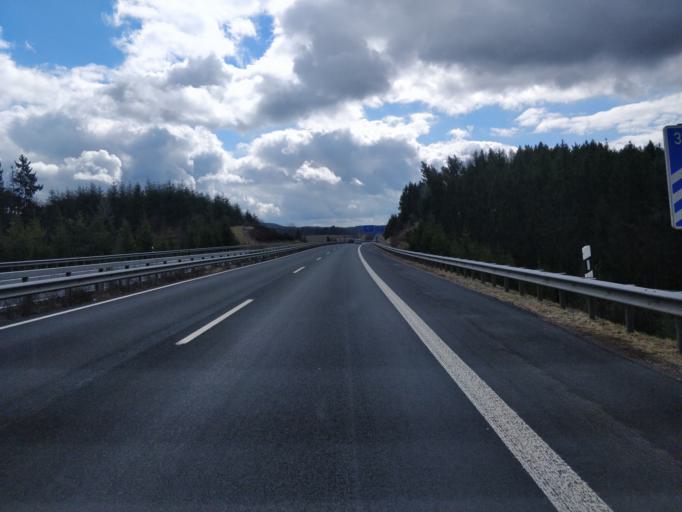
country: DE
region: Rheinland-Pfalz
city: Mehren
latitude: 50.1989
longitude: 6.8929
